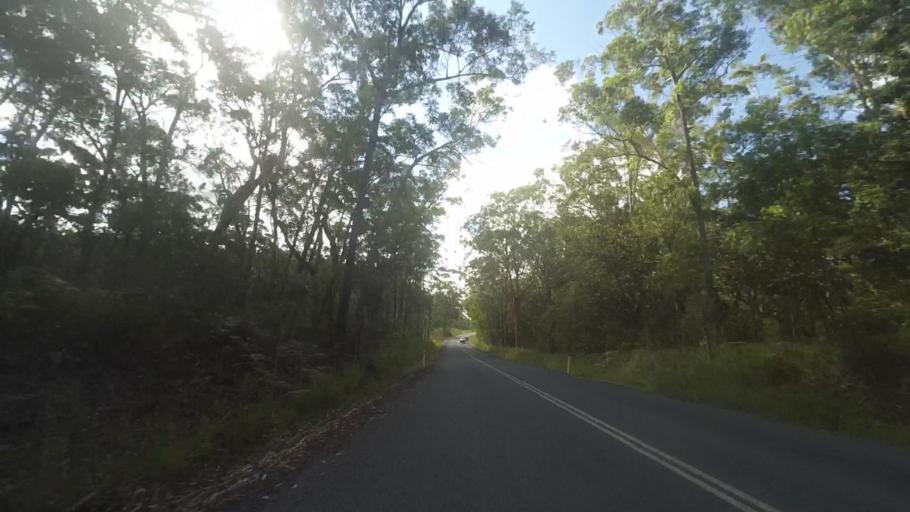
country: AU
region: New South Wales
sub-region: Great Lakes
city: Forster
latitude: -32.4244
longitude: 152.4988
